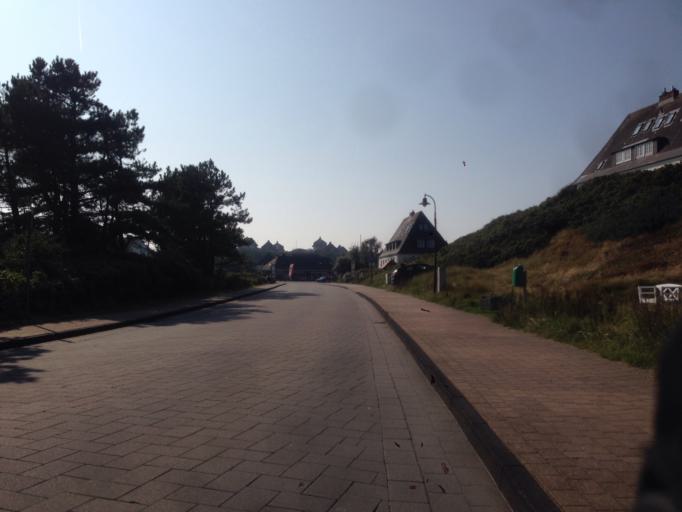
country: DE
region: Schleswig-Holstein
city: Norddorf
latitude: 54.7565
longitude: 8.2896
